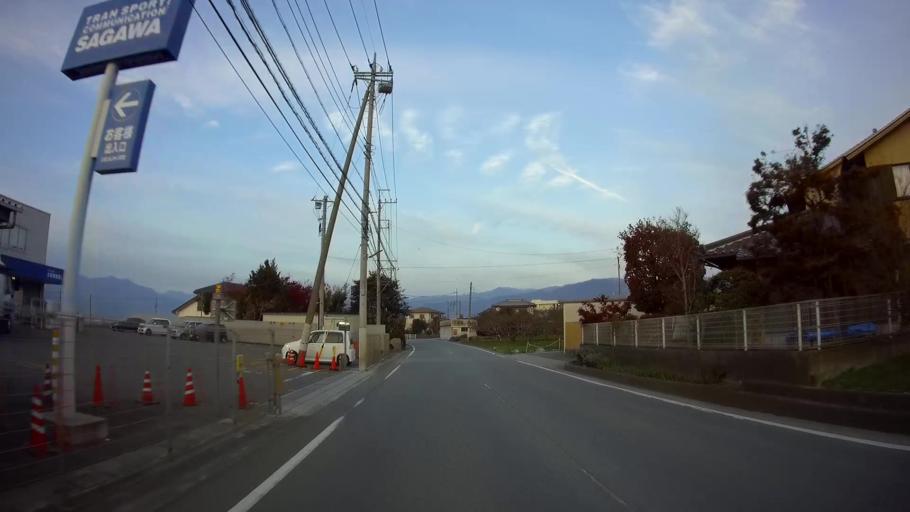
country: JP
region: Yamanashi
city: Isawa
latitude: 35.6331
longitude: 138.6842
